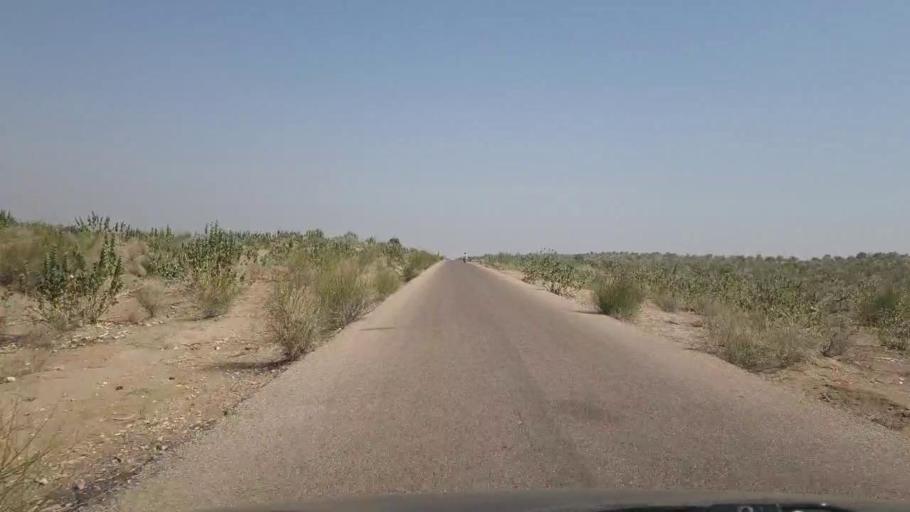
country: PK
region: Sindh
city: Chor
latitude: 25.6810
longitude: 70.1776
